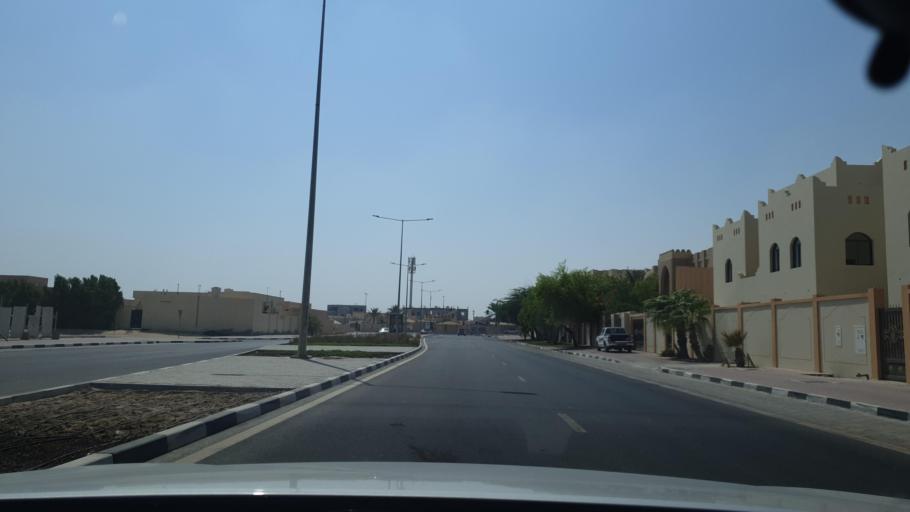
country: QA
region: Al Khawr
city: Al Khawr
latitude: 25.6819
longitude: 51.5161
